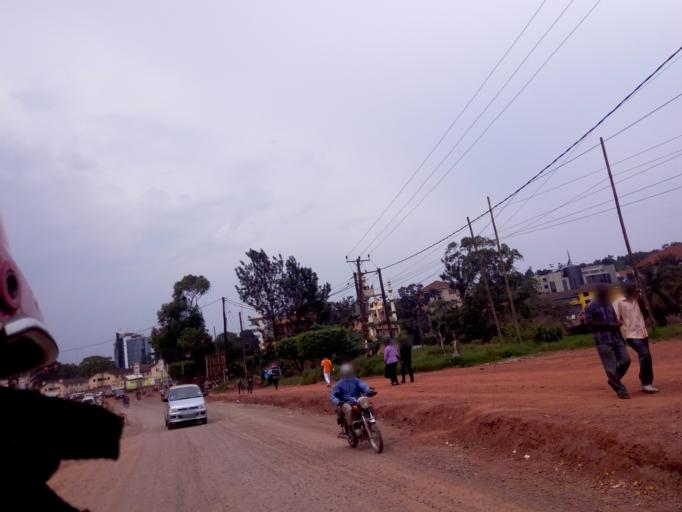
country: UG
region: Central Region
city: Kampala Central Division
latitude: 0.3295
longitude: 32.5728
